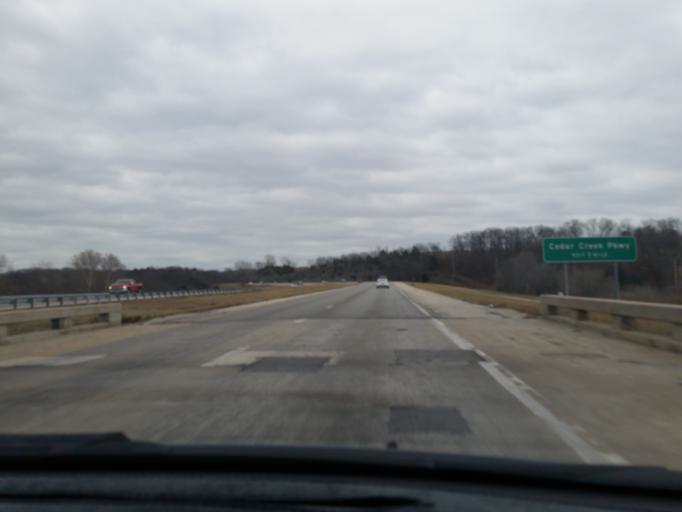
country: US
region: Kansas
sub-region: Johnson County
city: De Soto
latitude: 38.9505
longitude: -94.9053
